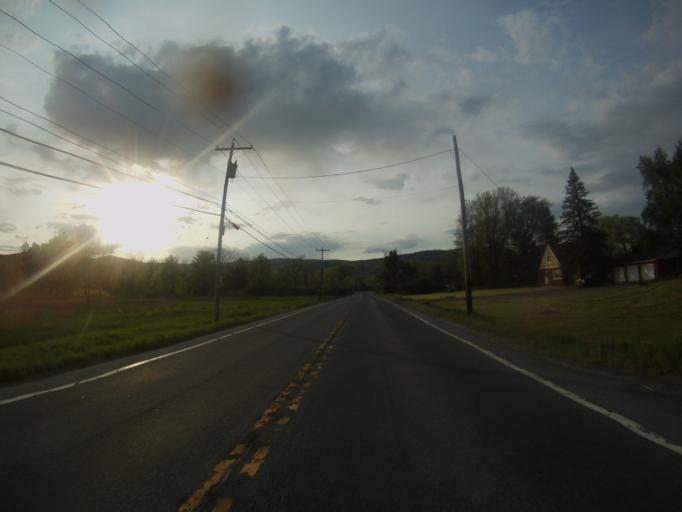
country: US
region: New York
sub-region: Essex County
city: Ticonderoga
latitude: 43.8690
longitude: -73.4407
